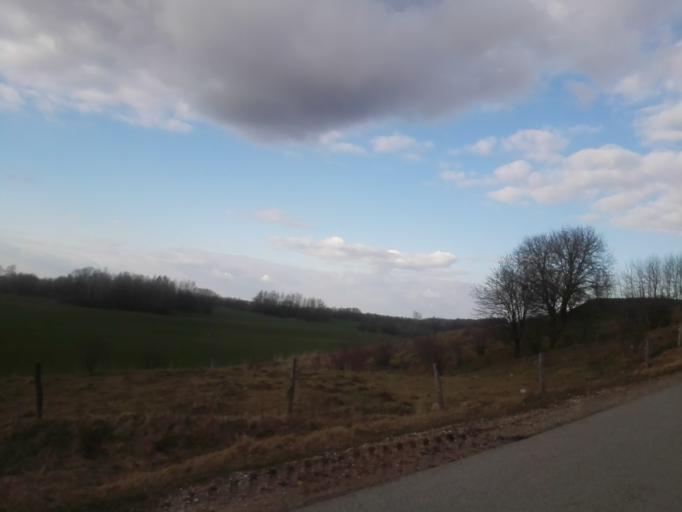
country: PL
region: Podlasie
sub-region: Suwalki
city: Suwalki
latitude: 54.2094
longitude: 22.9738
